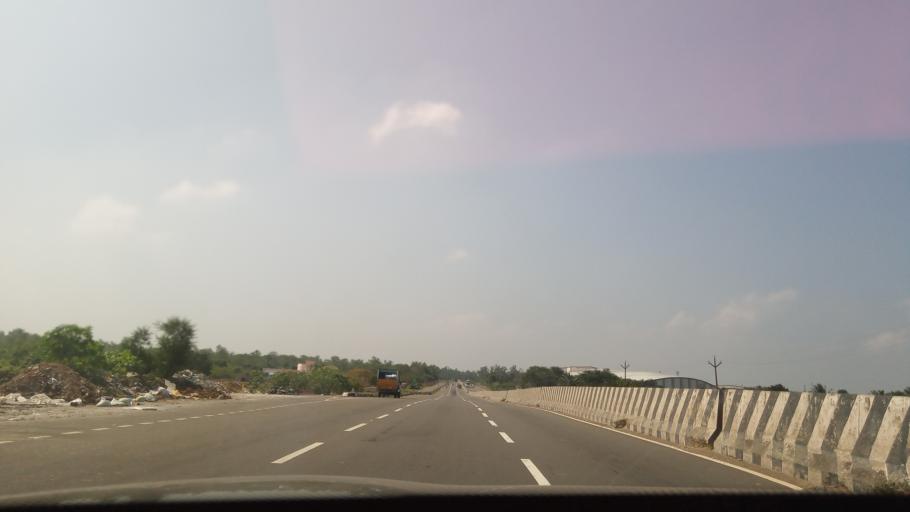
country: IN
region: Tamil Nadu
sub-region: Kancheepuram
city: Madambakkam
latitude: 12.8657
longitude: 79.9658
